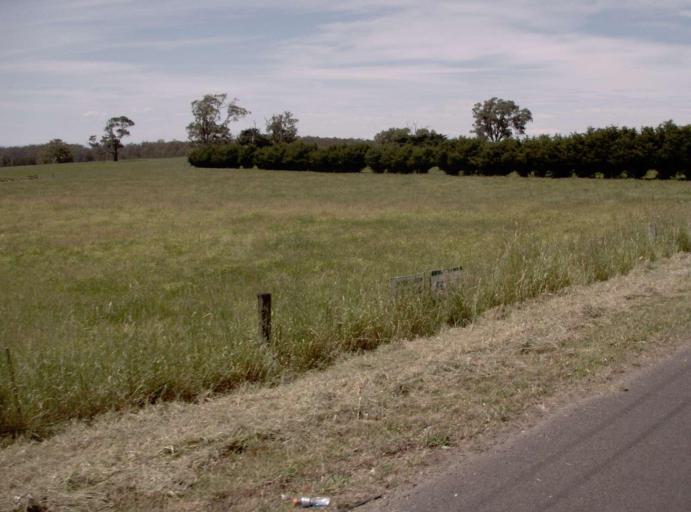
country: AU
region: Victoria
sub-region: Latrobe
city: Traralgon
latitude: -38.1729
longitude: 146.6644
